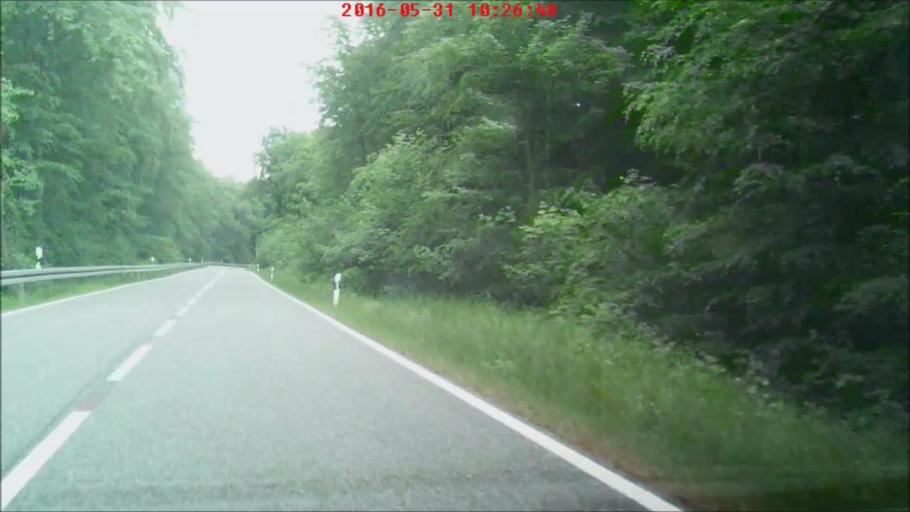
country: DE
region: Thuringia
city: Bad Frankenhausen
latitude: 51.3990
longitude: 11.0802
